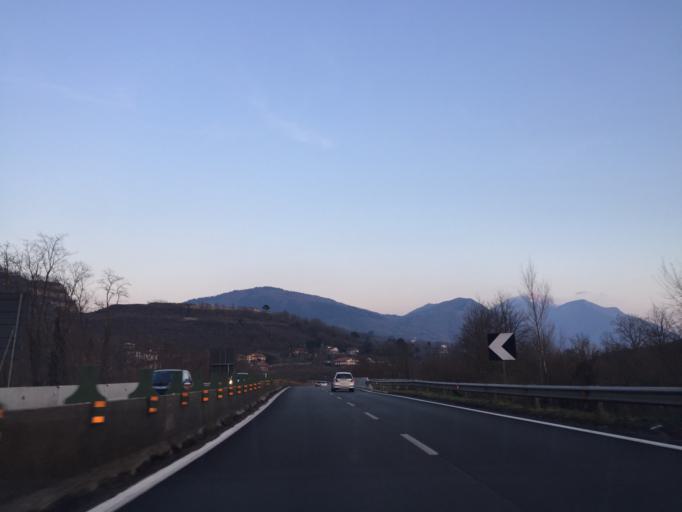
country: IT
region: Campania
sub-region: Provincia di Avellino
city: Atripalda
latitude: 40.9104
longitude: 14.8280
